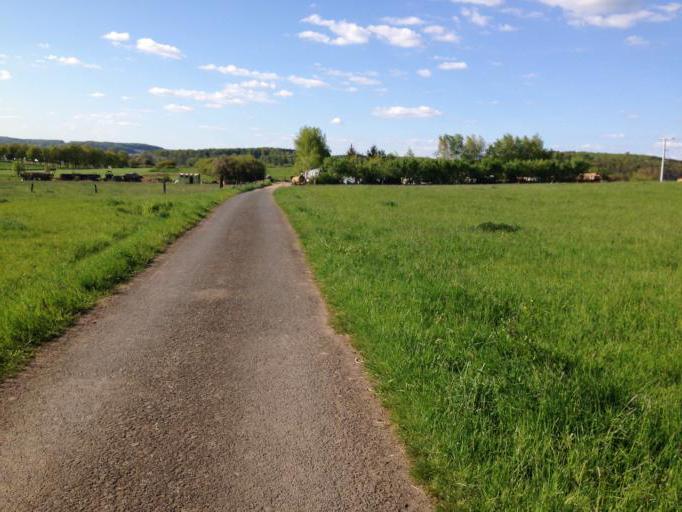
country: DE
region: Hesse
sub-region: Regierungsbezirk Giessen
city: Reiskirchen
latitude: 50.5819
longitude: 8.8176
